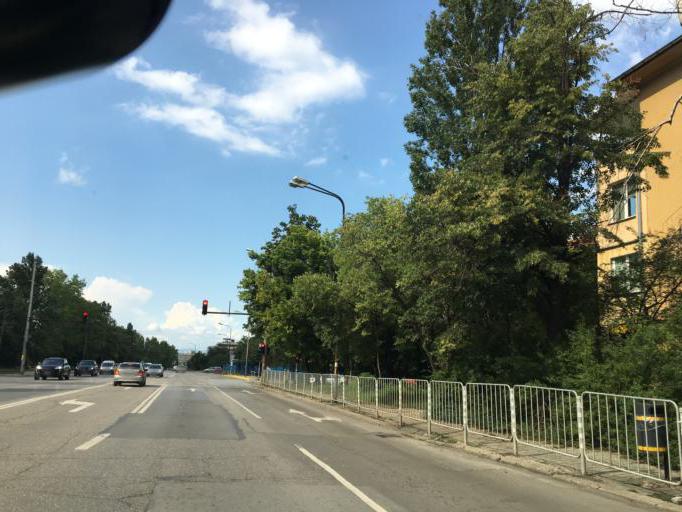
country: BG
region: Sofia-Capital
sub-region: Stolichna Obshtina
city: Sofia
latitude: 42.6568
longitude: 23.3592
